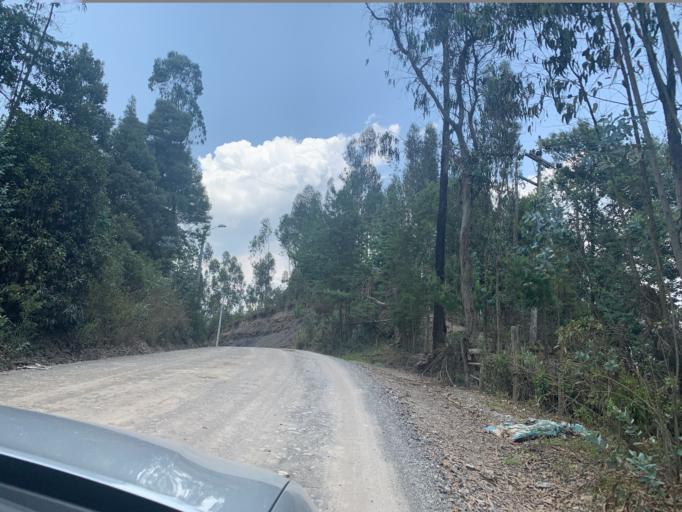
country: CO
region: Boyaca
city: Chiquinquira
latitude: 5.5977
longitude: -73.7622
